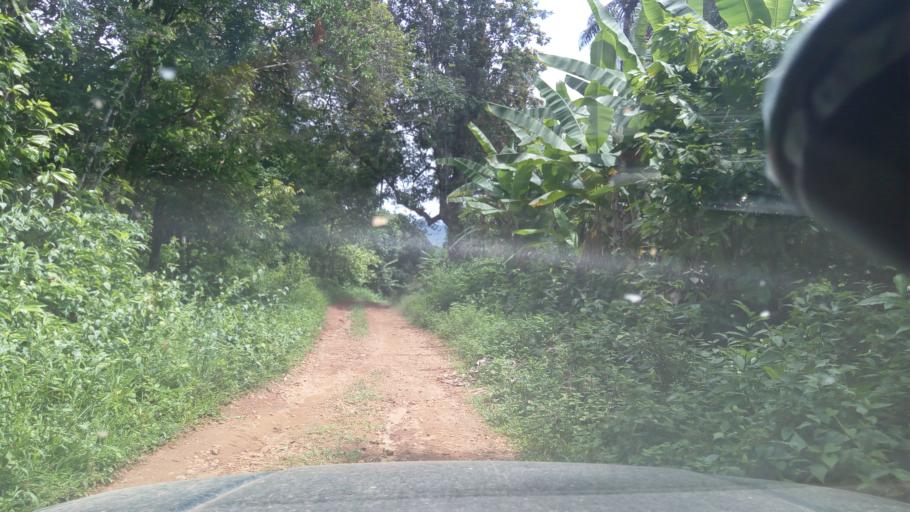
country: SL
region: Eastern Province
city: Segbwema
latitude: 8.1010
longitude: -11.0047
